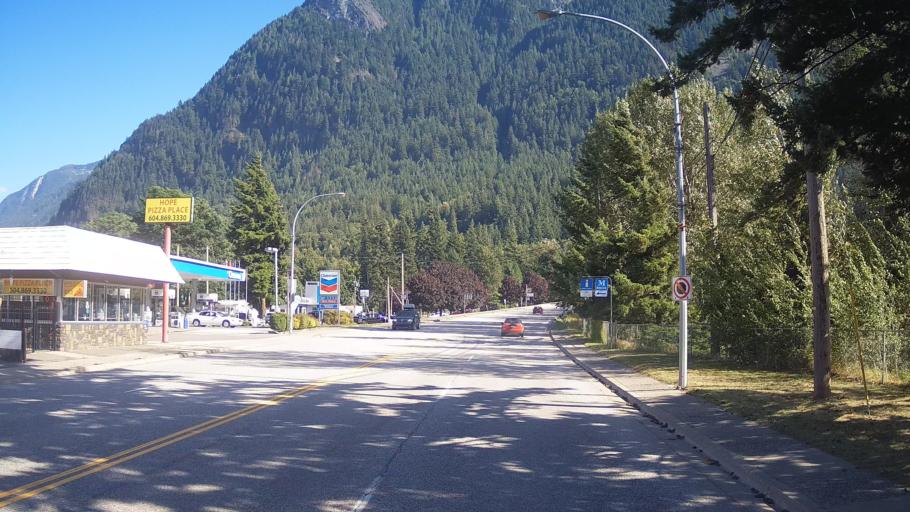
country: CA
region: British Columbia
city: Hope
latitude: 49.3776
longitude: -121.4437
